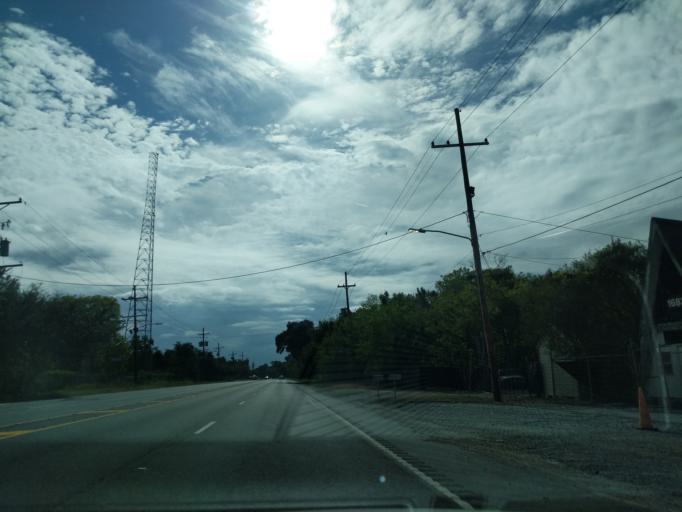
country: US
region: Louisiana
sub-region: Saint Bernard Parish
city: Meraux
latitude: 30.0485
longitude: -89.8865
